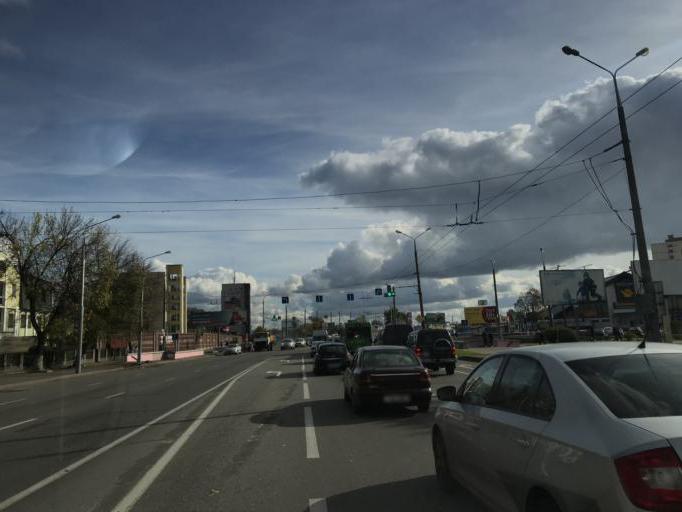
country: BY
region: Gomel
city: Gomel
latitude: 52.4480
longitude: 30.9697
